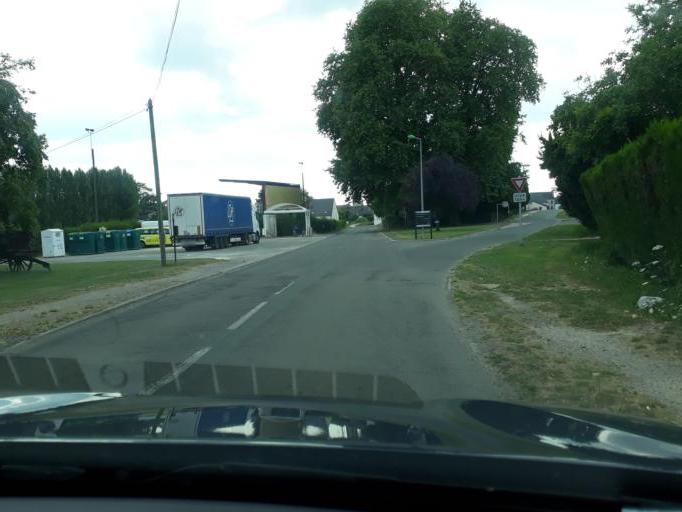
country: FR
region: Centre
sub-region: Departement du Cher
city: Baugy
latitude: 47.0817
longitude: 2.7332
